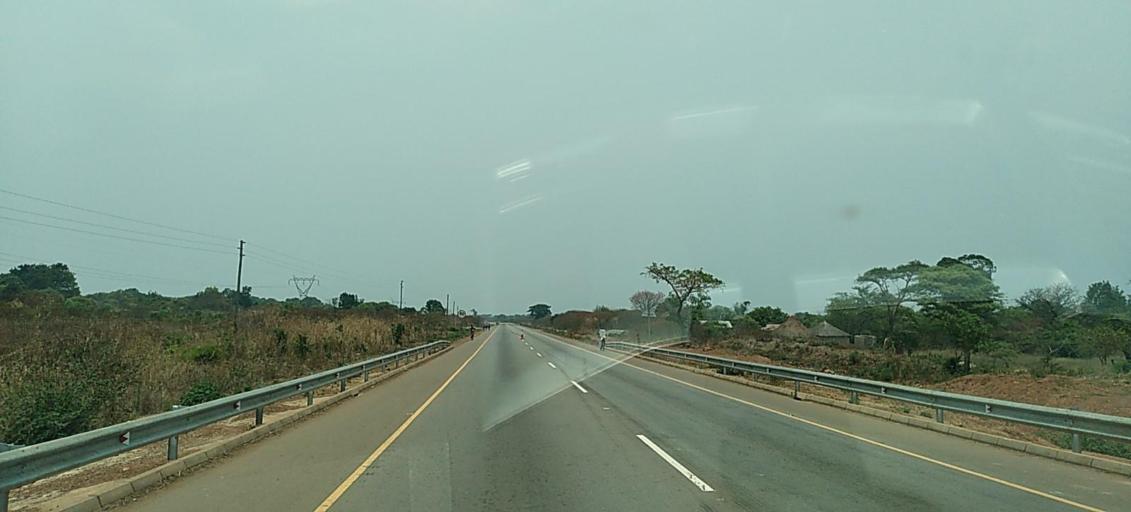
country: ZM
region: Copperbelt
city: Chililabombwe
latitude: -12.3825
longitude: 27.3246
